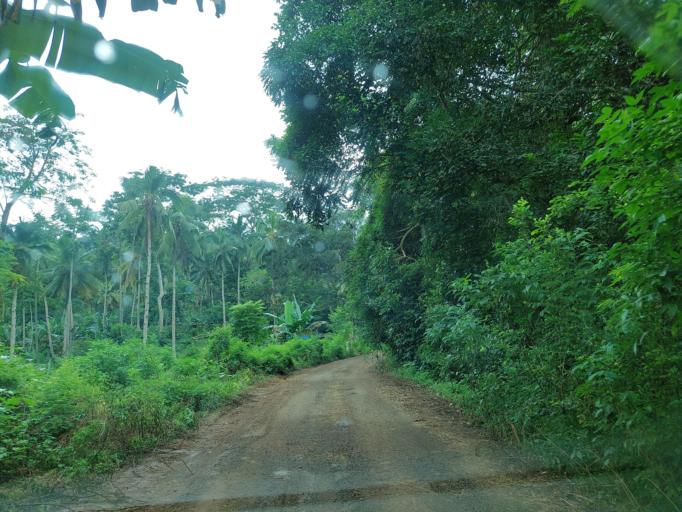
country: YT
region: Tsingoni
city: Tsingoni
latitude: -12.7622
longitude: 45.1232
